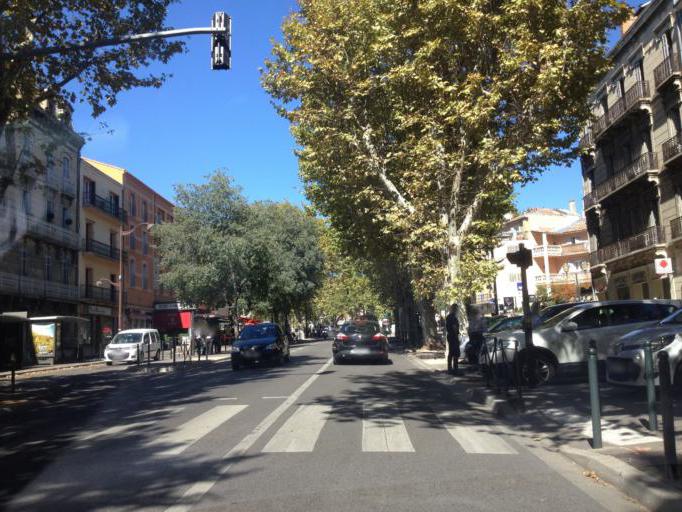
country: FR
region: Provence-Alpes-Cote d'Azur
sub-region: Departement des Bouches-du-Rhone
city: Aix-en-Provence
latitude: 43.5246
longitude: 5.4465
